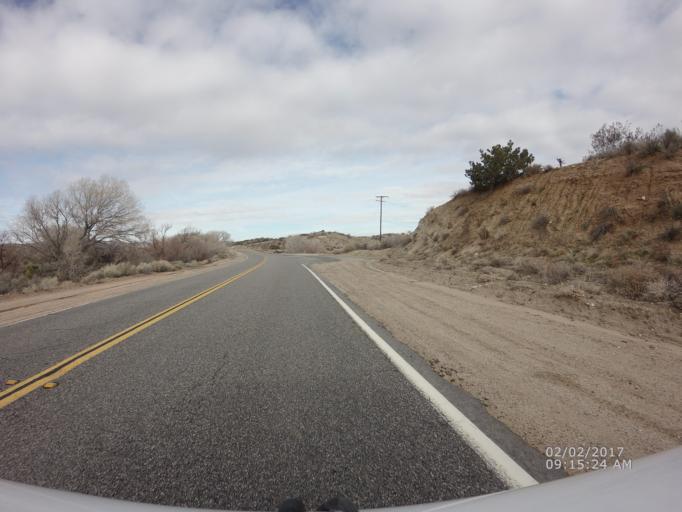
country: US
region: California
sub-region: Los Angeles County
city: Vincent
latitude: 34.5264
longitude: -118.0537
